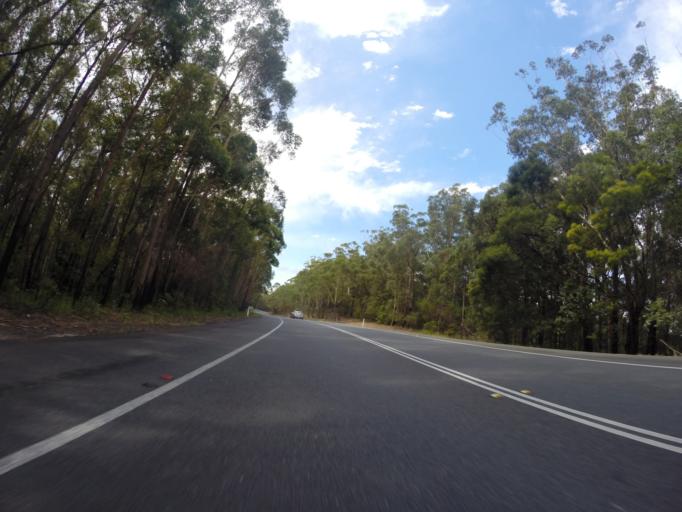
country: AU
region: New South Wales
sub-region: Shoalhaven Shire
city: Milton
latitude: -35.1639
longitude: 150.4459
